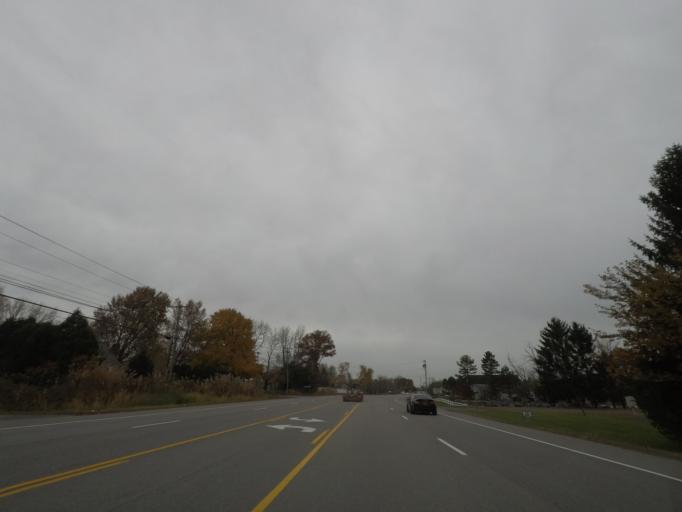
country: US
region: New York
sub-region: Albany County
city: Cohoes
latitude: 42.8022
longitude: -73.7335
